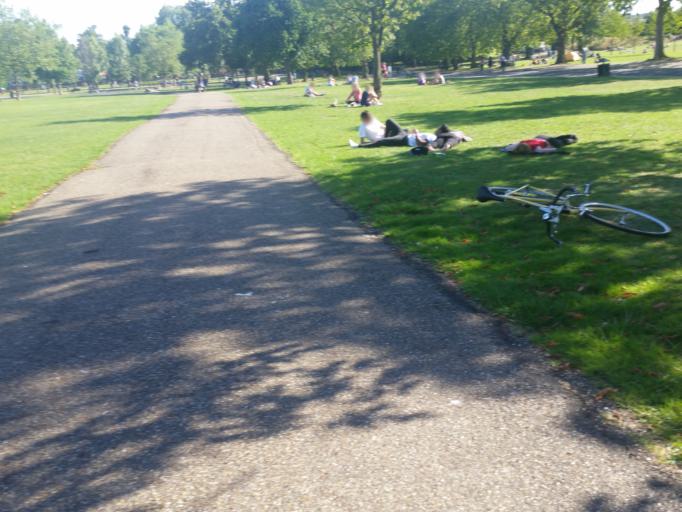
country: GB
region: England
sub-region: Greater London
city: Harringay
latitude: 51.5679
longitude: -0.1033
